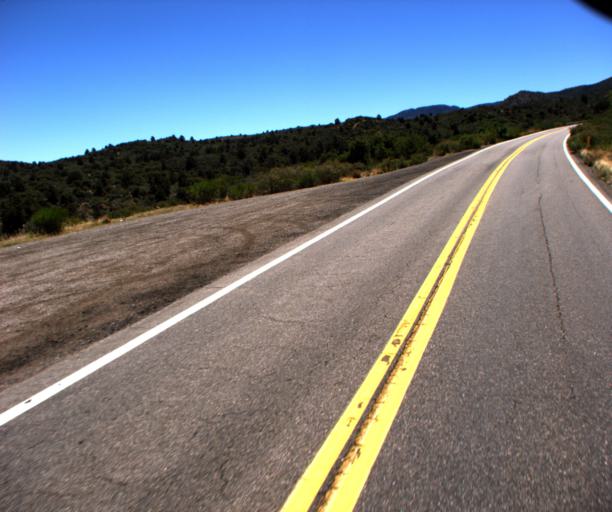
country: US
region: Arizona
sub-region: Gila County
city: Globe
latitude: 33.2883
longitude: -110.7505
